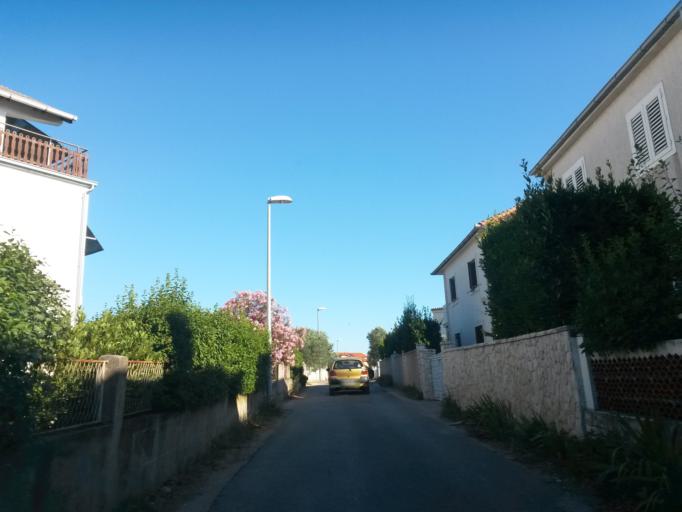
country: HR
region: Sibensko-Kniniska
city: Rogoznica
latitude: 43.5392
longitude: 15.9608
